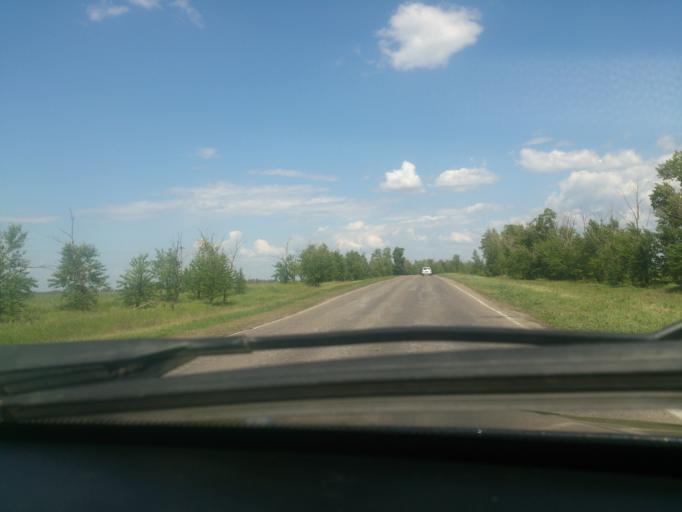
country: RU
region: Ulyanovsk
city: Cherdakly
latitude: 54.3953
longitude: 48.8542
